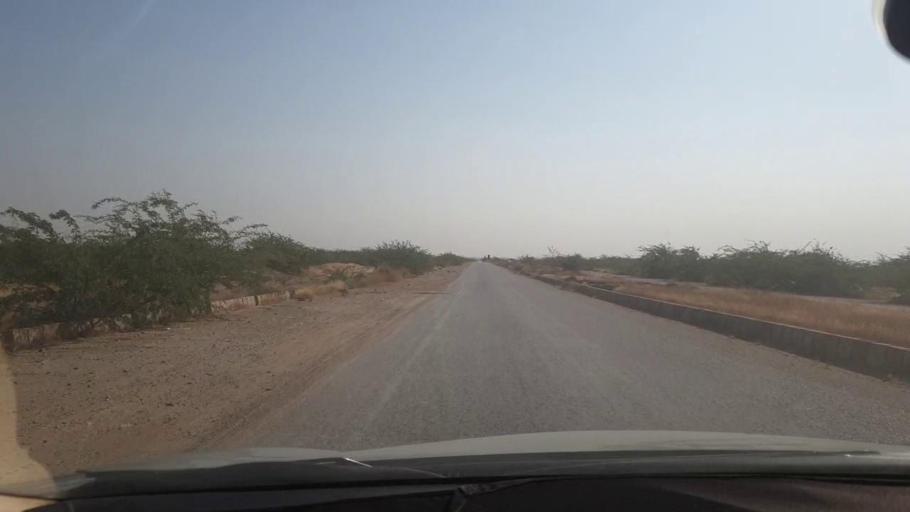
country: PK
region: Sindh
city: Malir Cantonment
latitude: 25.0757
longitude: 67.1384
